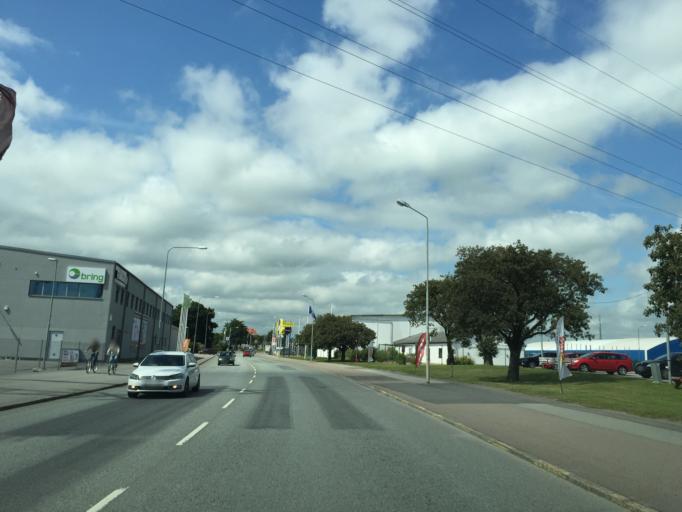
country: SE
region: Skane
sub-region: Ystads Kommun
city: Ystad
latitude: 55.4357
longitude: 13.8379
